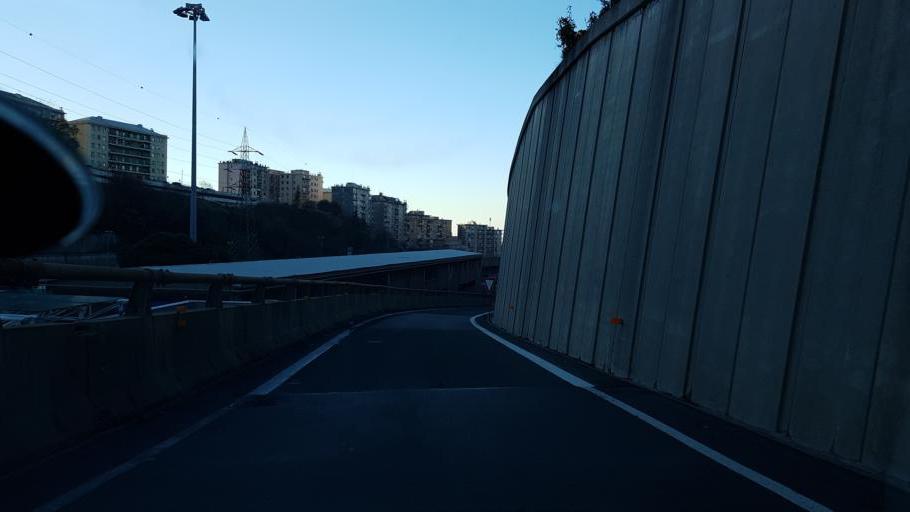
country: IT
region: Liguria
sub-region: Provincia di Genova
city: San Teodoro
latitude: 44.4222
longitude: 8.8671
